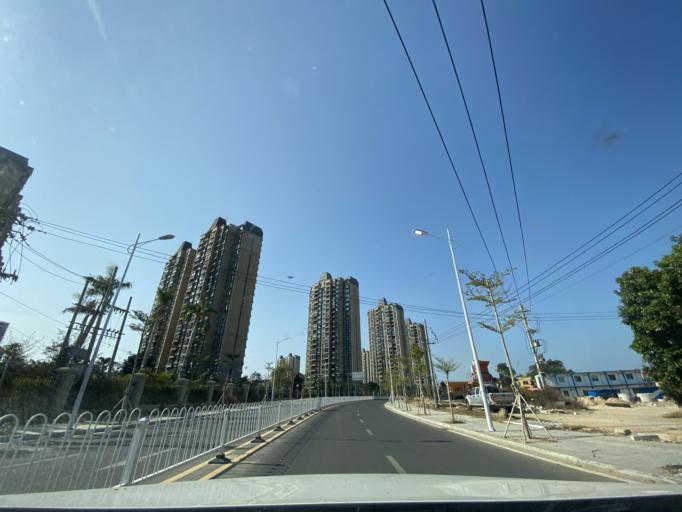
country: CN
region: Hainan
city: Yingzhou
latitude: 18.4141
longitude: 109.8543
